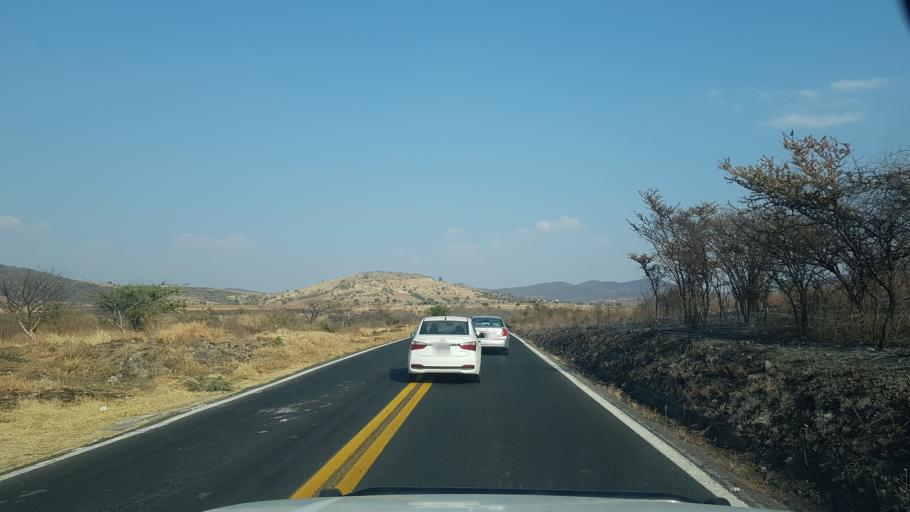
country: MX
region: Puebla
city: Calmeca
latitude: 18.6537
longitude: -98.6474
